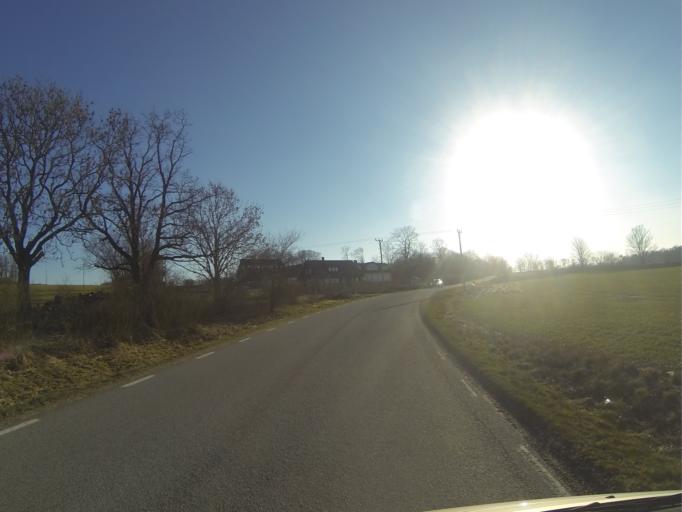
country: SE
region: Skane
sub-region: Horby Kommun
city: Hoerby
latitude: 55.8422
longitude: 13.6340
